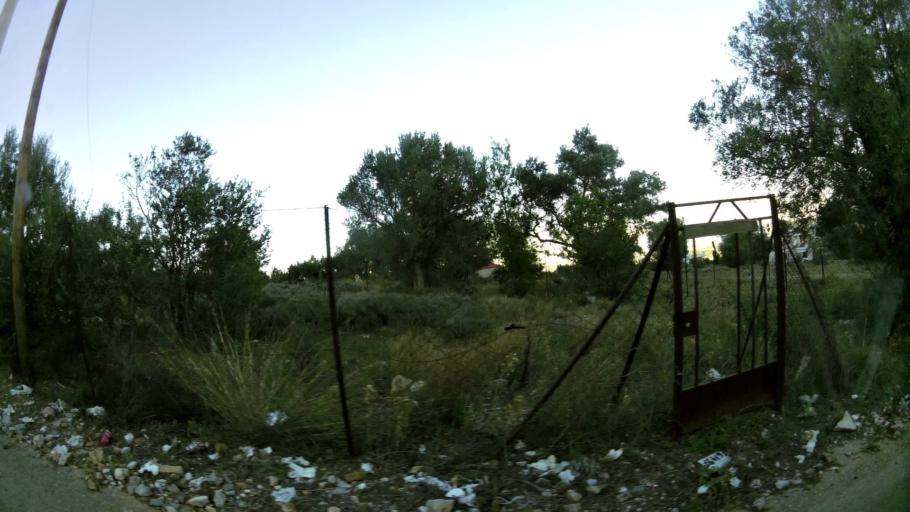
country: GR
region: Attica
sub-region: Nomarchia Anatolikis Attikis
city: Paiania
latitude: 37.9705
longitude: 23.8379
